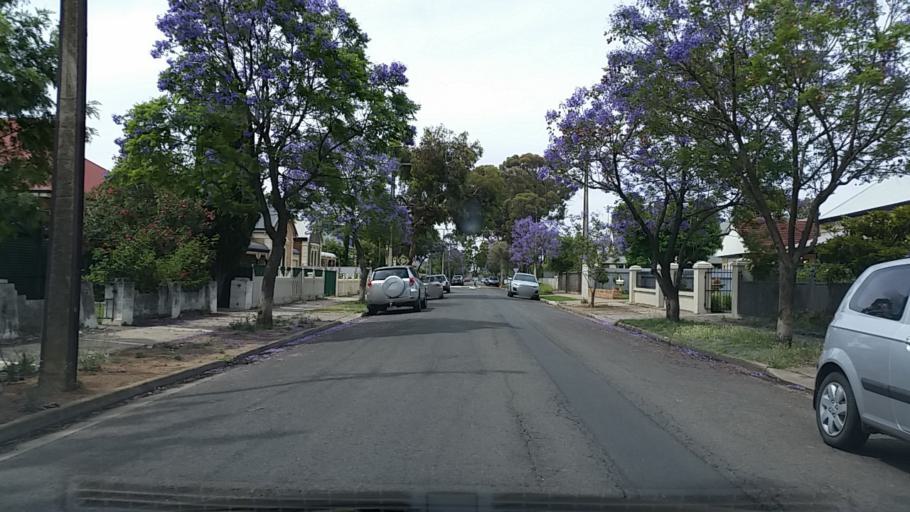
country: AU
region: South Australia
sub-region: Charles Sturt
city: Allenby Gardens
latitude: -34.8953
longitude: 138.5654
